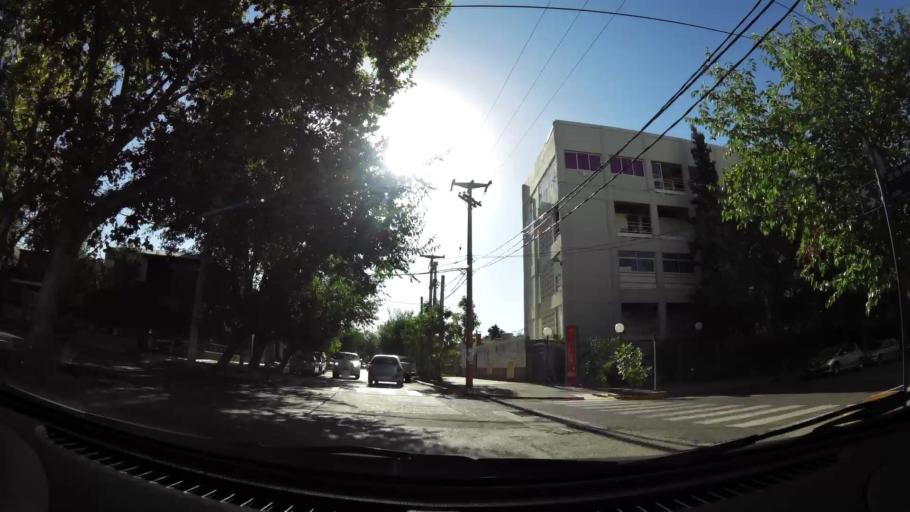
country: AR
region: Mendoza
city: Mendoza
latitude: -32.9001
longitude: -68.8101
